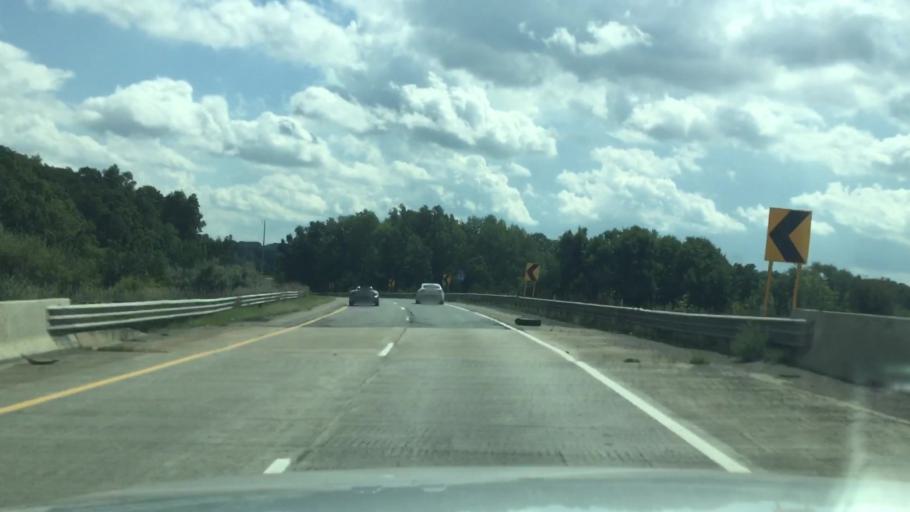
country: US
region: Michigan
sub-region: Washtenaw County
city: Chelsea
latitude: 42.2932
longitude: -84.0879
